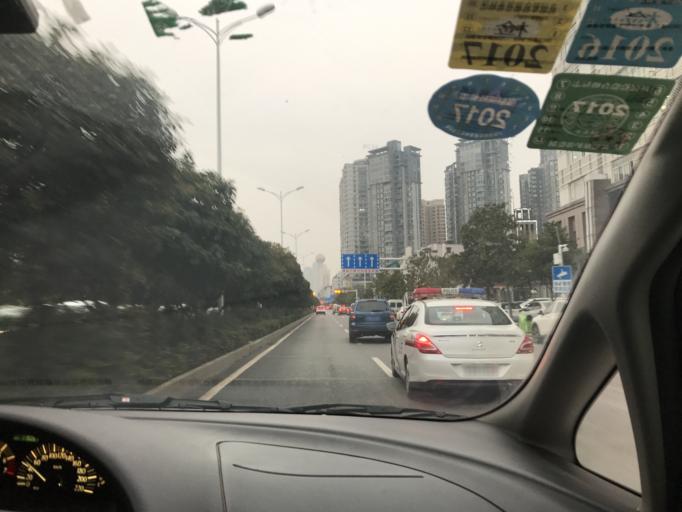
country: CN
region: Hubei
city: Jiang'an
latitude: 30.6069
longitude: 114.3074
